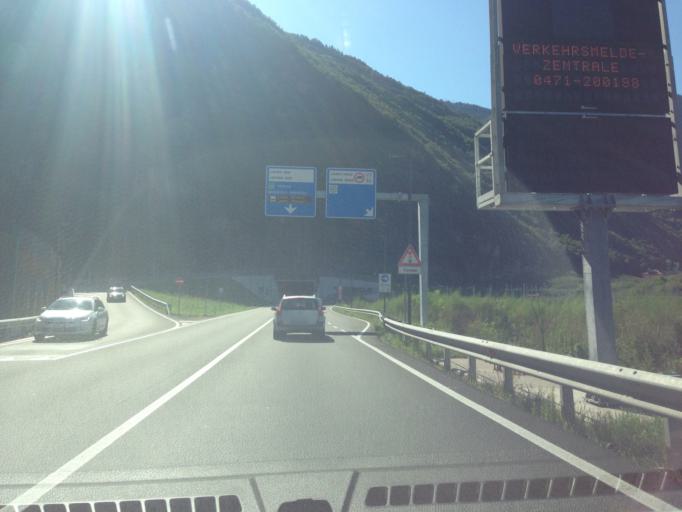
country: IT
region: Trentino-Alto Adige
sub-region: Bolzano
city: Pineta
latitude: 46.4357
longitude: 11.3456
